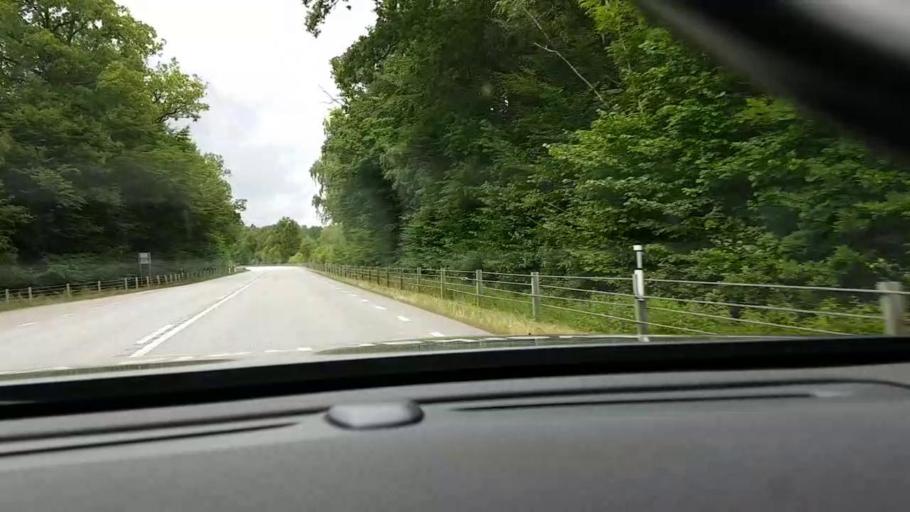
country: SE
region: Skane
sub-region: Horby Kommun
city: Hoerby
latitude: 55.8836
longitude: 13.6307
